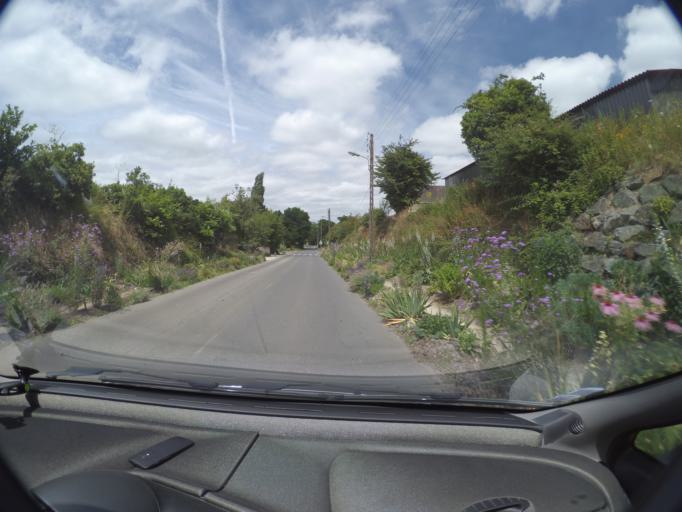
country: FR
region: Pays de la Loire
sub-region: Departement de la Loire-Atlantique
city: Gorges
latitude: 47.1037
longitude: -1.3044
